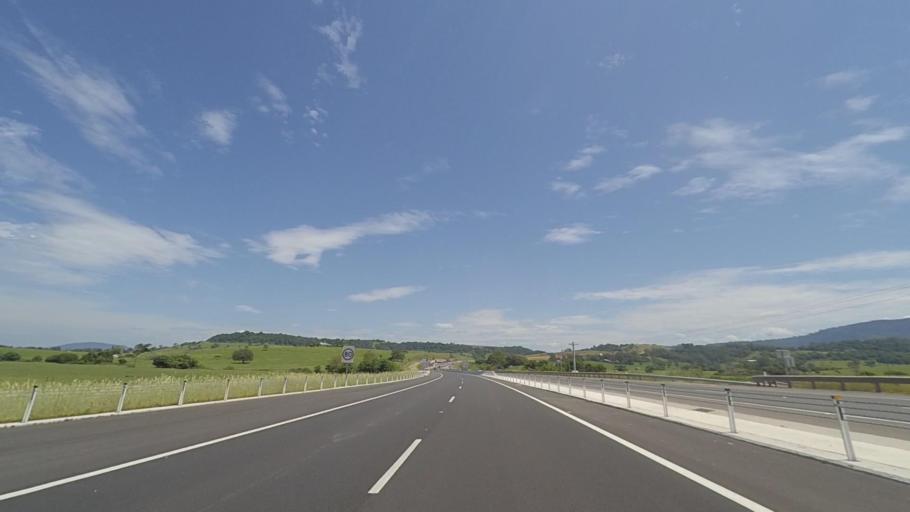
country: AU
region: New South Wales
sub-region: Kiama
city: Gerringong
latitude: -34.7498
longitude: 150.7901
